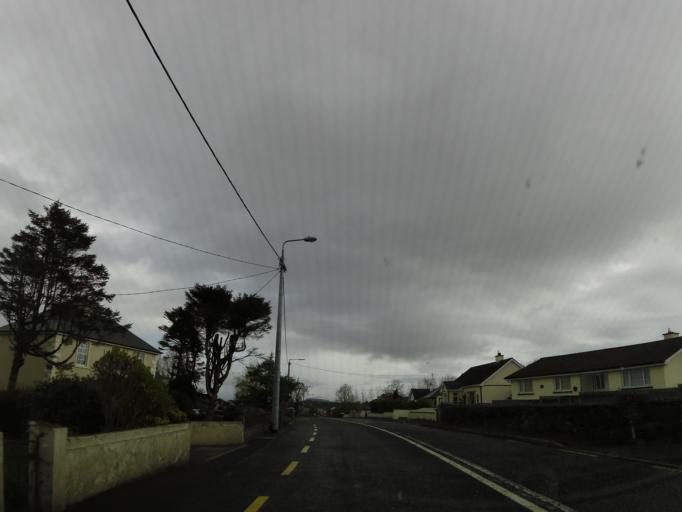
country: IE
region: Connaught
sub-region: Sligo
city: Tobercurry
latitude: 54.0468
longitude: -8.7378
